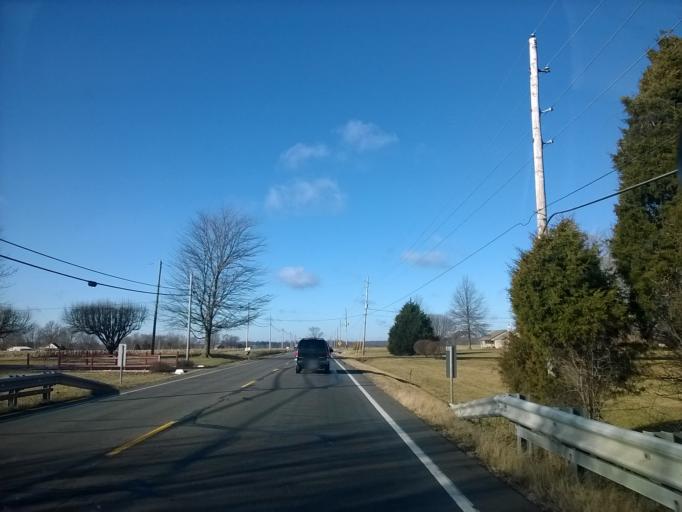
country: US
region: Indiana
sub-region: Jefferson County
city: Hanover
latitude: 38.7127
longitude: -85.5102
